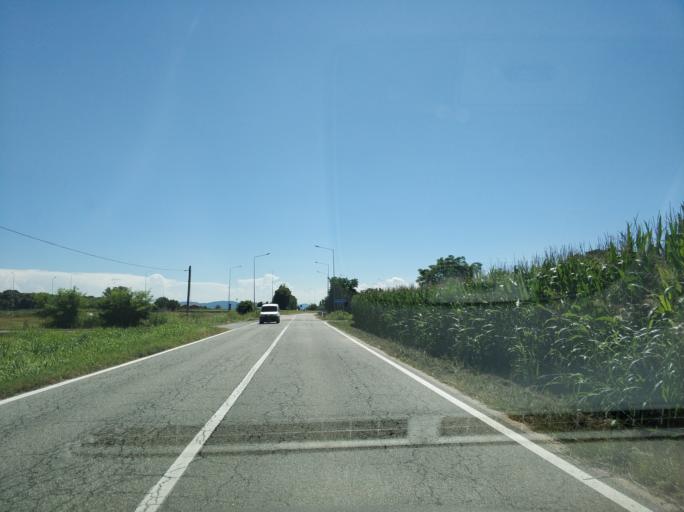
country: IT
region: Piedmont
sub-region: Provincia di Vercelli
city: Cigliano
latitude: 45.2995
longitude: 8.0077
